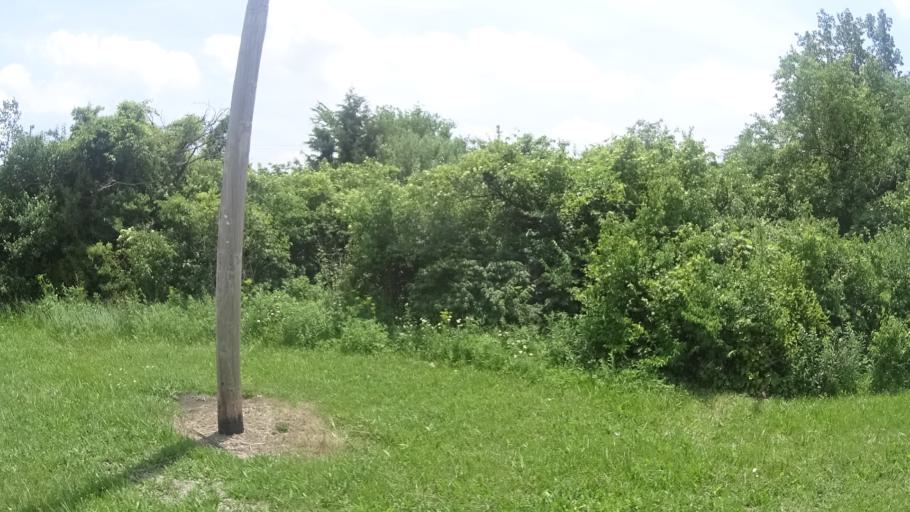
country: US
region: Ohio
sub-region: Huron County
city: Bellevue
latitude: 41.2982
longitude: -82.7690
